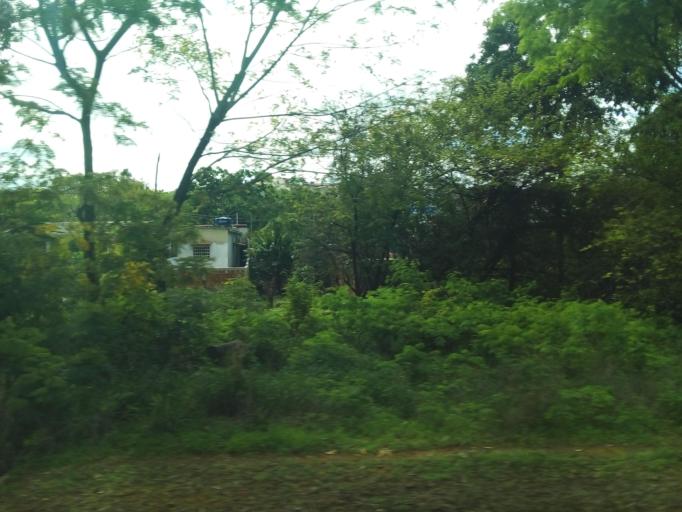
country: BR
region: Minas Gerais
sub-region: Governador Valadares
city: Governador Valadares
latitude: -18.8862
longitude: -41.9710
